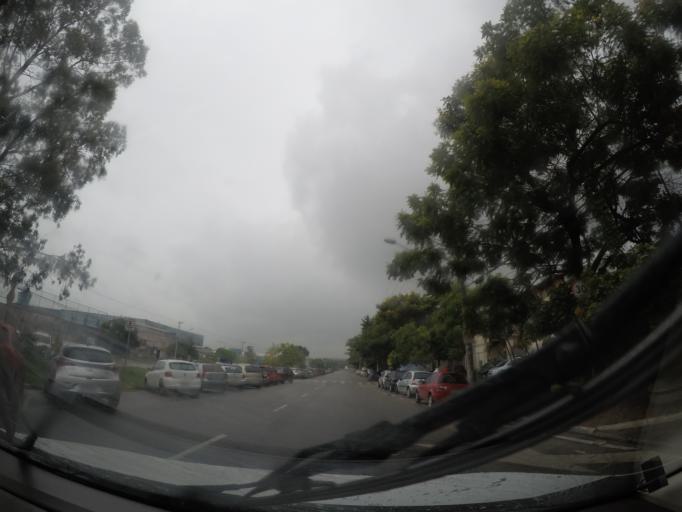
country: BR
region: Sao Paulo
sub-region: Guarulhos
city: Guarulhos
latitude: -23.4387
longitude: -46.5018
